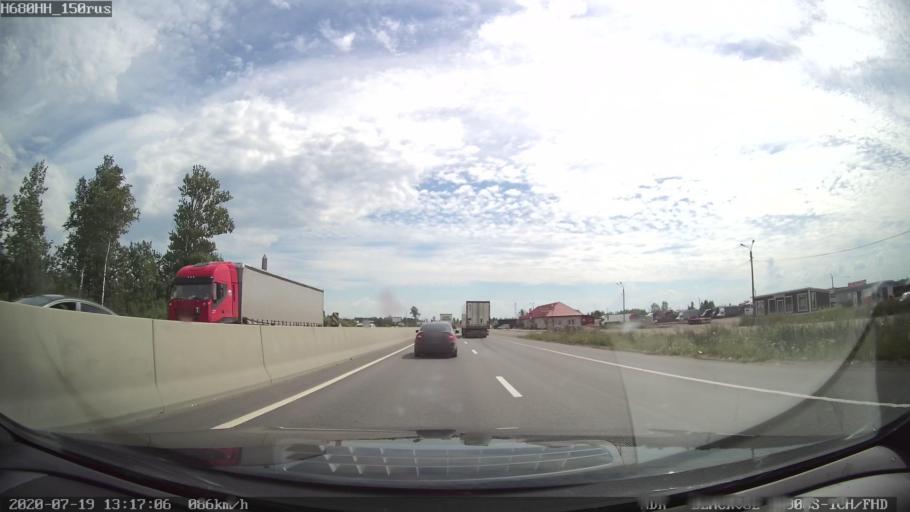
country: RU
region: St.-Petersburg
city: Kolpino
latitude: 59.7116
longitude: 30.5649
